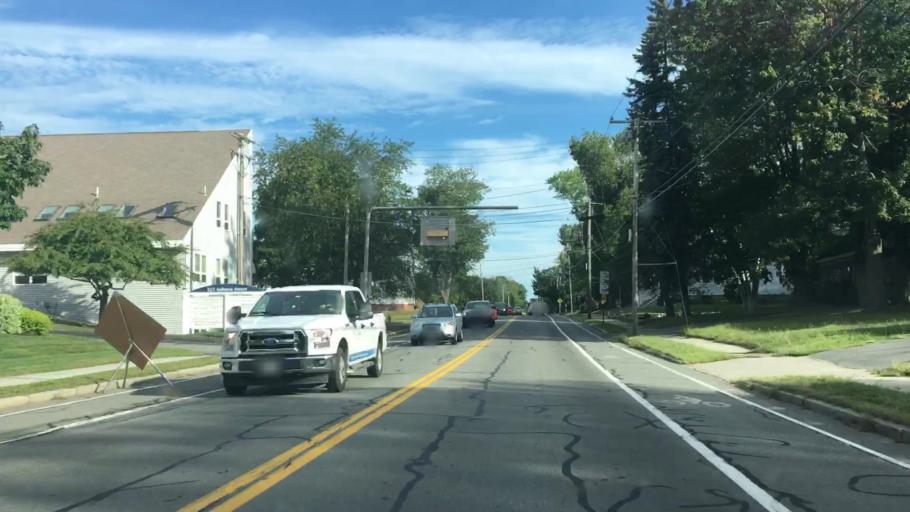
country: US
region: Maine
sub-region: Cumberland County
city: Falmouth
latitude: 43.7077
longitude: -70.2904
